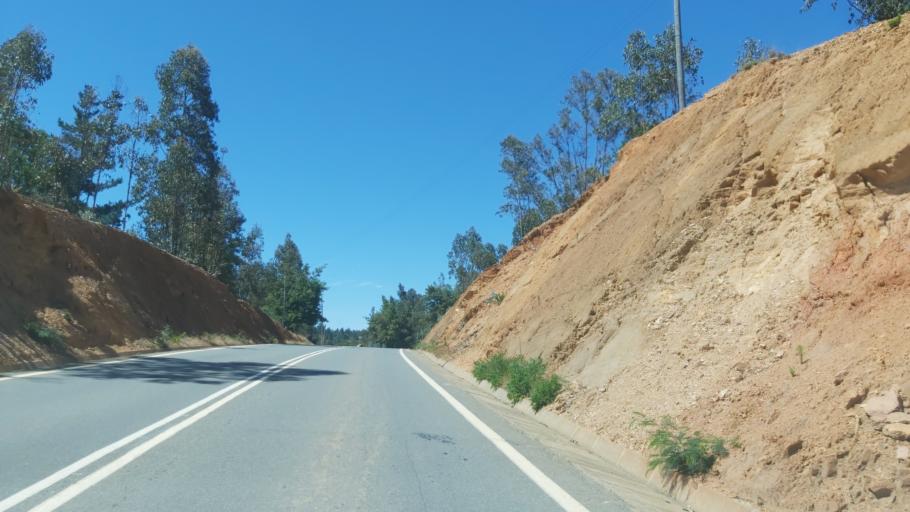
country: CL
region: Maule
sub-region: Provincia de Talca
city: Constitucion
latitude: -34.9177
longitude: -71.9925
